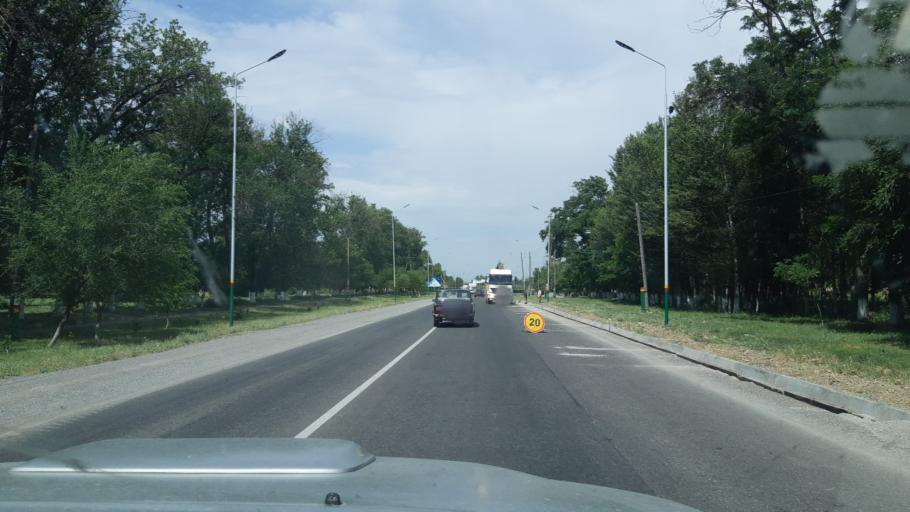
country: KZ
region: Ongtustik Qazaqstan
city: Turar Ryskulov
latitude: 42.5489
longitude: 70.3100
